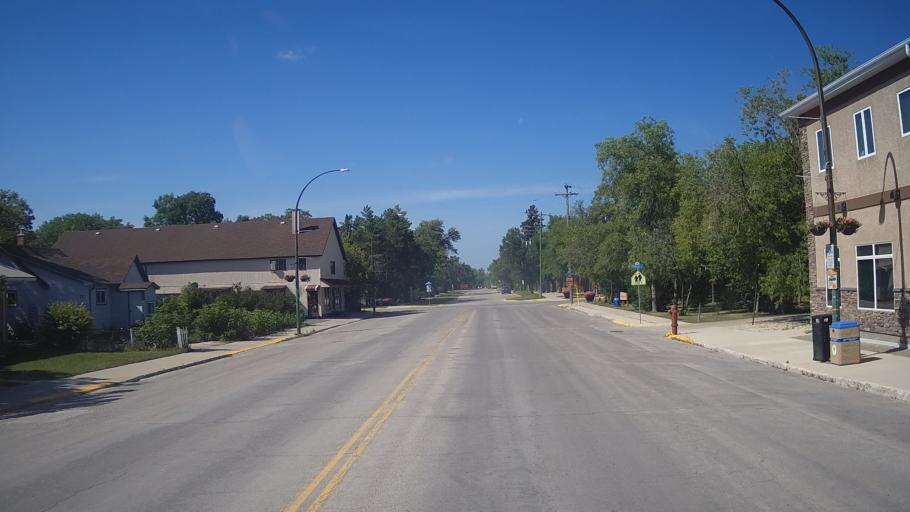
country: CA
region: Manitoba
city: Stonewall
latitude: 50.1367
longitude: -97.3266
